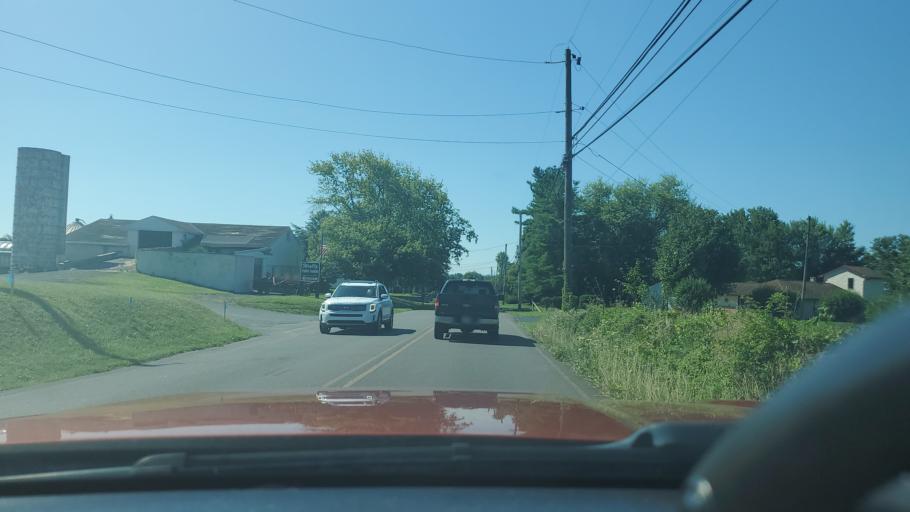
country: US
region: Pennsylvania
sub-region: Montgomery County
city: Limerick
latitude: 40.2409
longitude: -75.5285
